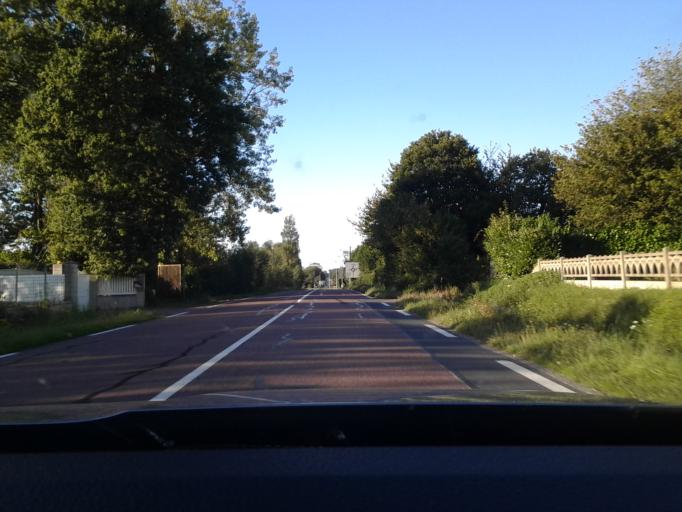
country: FR
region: Lower Normandy
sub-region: Departement de la Manche
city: La Haye-du-Puits
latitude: 49.3027
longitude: -1.5422
